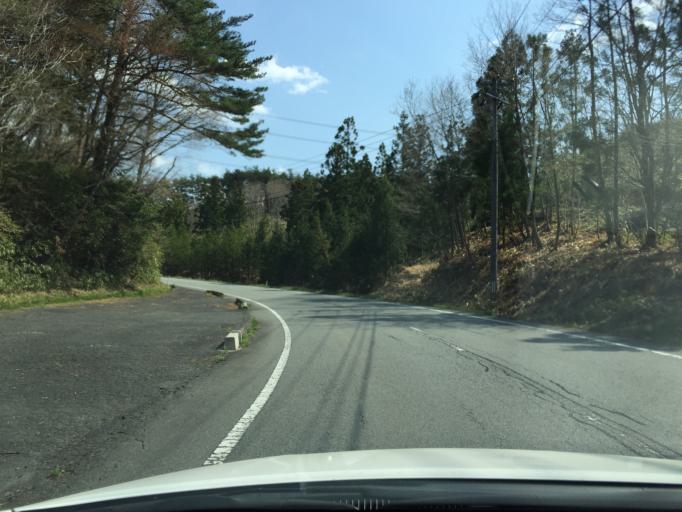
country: JP
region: Fukushima
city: Namie
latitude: 37.3831
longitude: 140.7992
